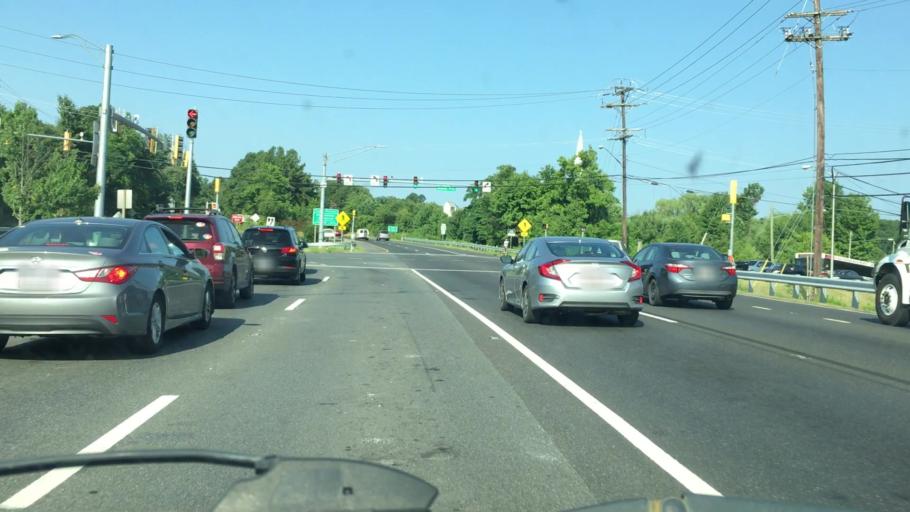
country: US
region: Maryland
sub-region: Prince George's County
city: College Park
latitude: 39.0006
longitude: -76.9425
